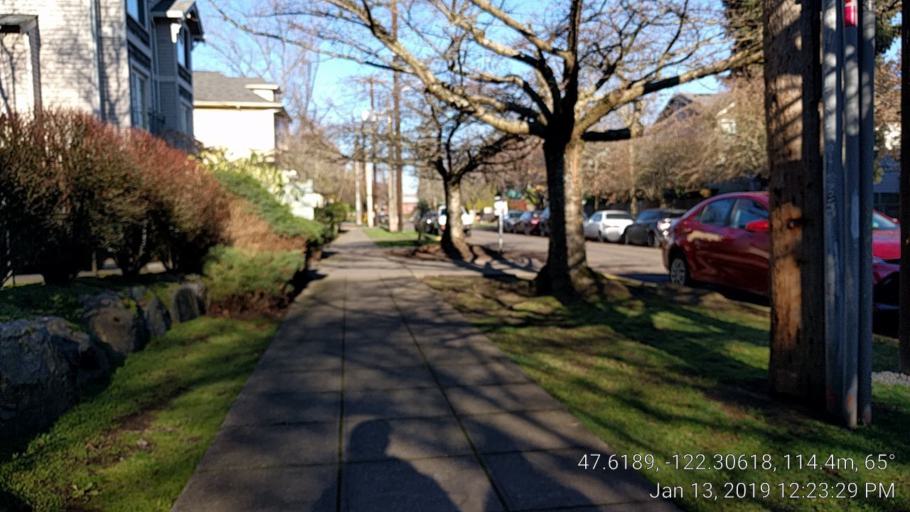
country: US
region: Washington
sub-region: King County
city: Seattle
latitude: 47.6190
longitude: -122.3062
